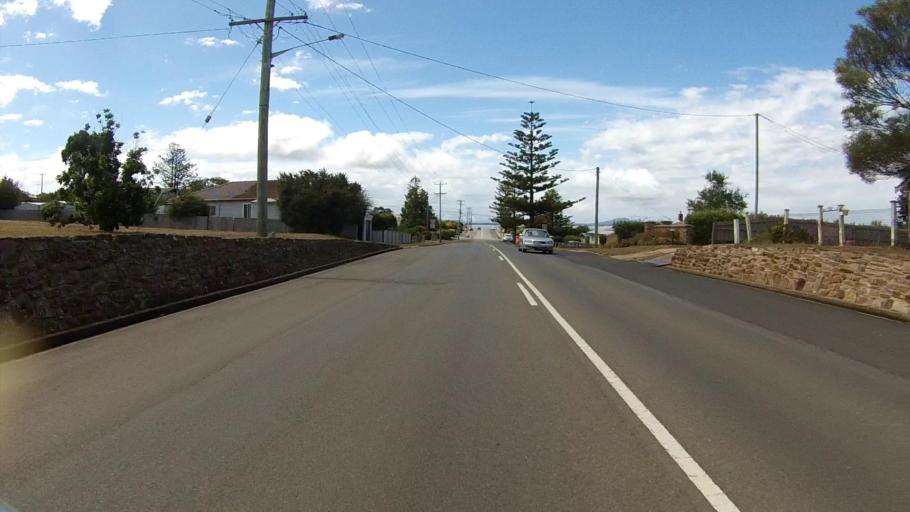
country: AU
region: Tasmania
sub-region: Break O'Day
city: St Helens
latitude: -42.1274
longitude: 148.0750
